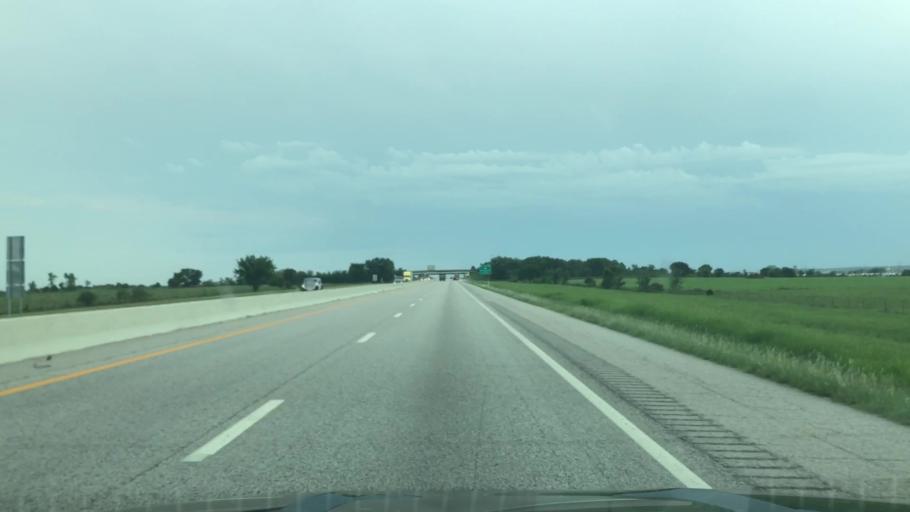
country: US
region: Oklahoma
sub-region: Craig County
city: Vinita
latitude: 36.5732
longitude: -95.2097
